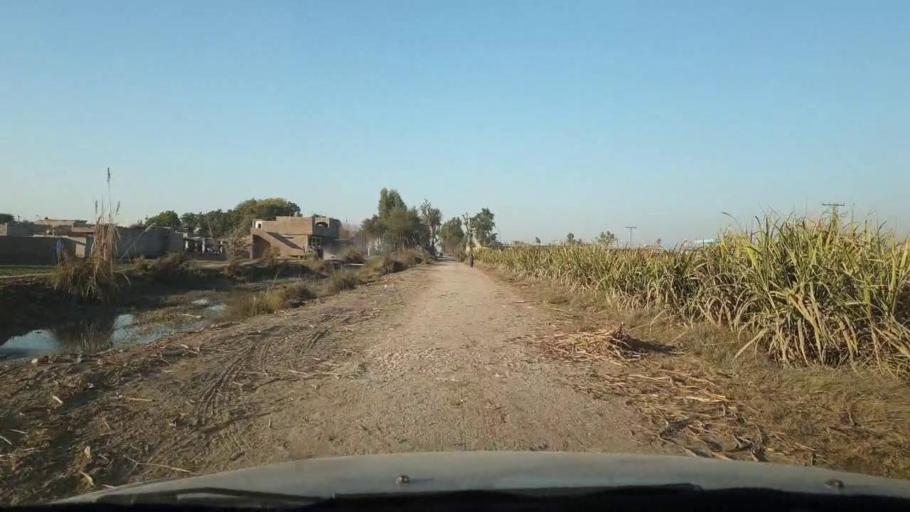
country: PK
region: Sindh
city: Ghotki
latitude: 27.9928
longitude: 69.2724
